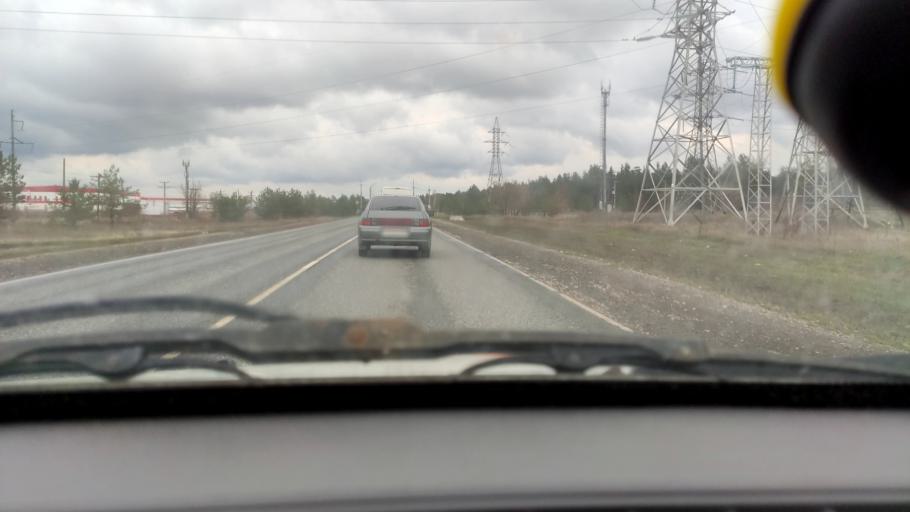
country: RU
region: Samara
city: Zhigulevsk
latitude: 53.5611
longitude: 49.5413
